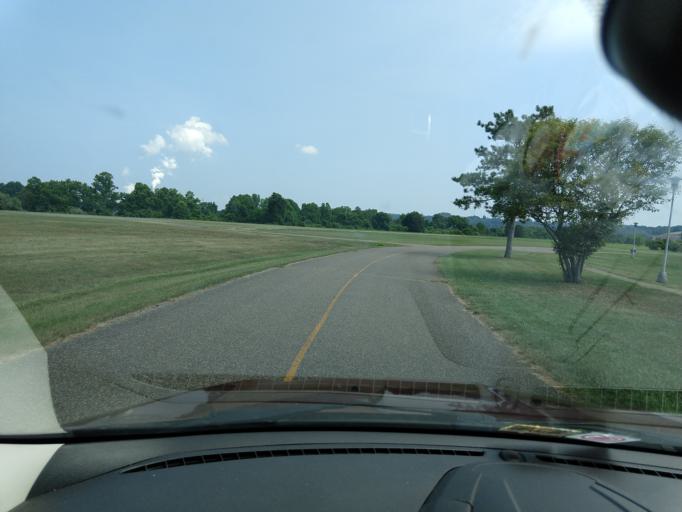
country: US
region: West Virginia
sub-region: Mason County
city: New Haven
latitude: 38.9238
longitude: -81.9087
